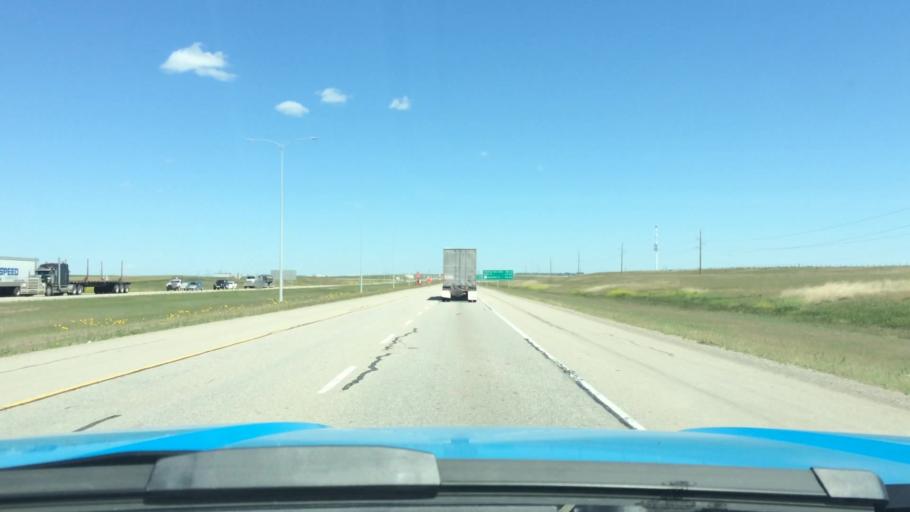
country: CA
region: Alberta
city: Chestermere
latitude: 51.1416
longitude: -113.9211
